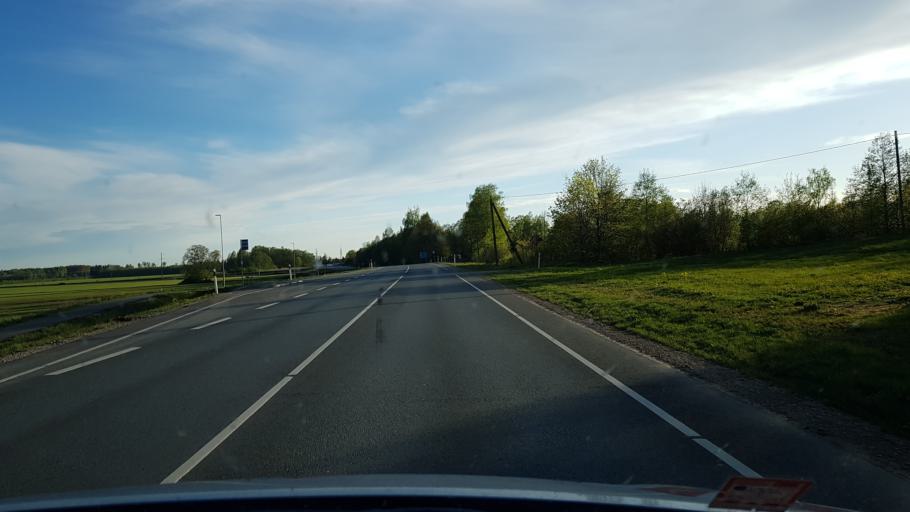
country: EE
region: Paernumaa
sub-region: Tootsi vald
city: Tootsi
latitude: 58.5081
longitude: 24.8035
